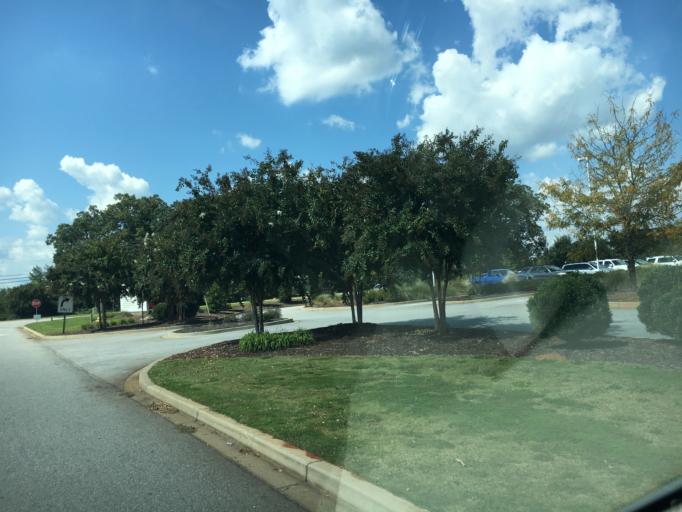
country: US
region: South Carolina
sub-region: Anderson County
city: Powdersville
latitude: 34.7892
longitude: -82.4807
